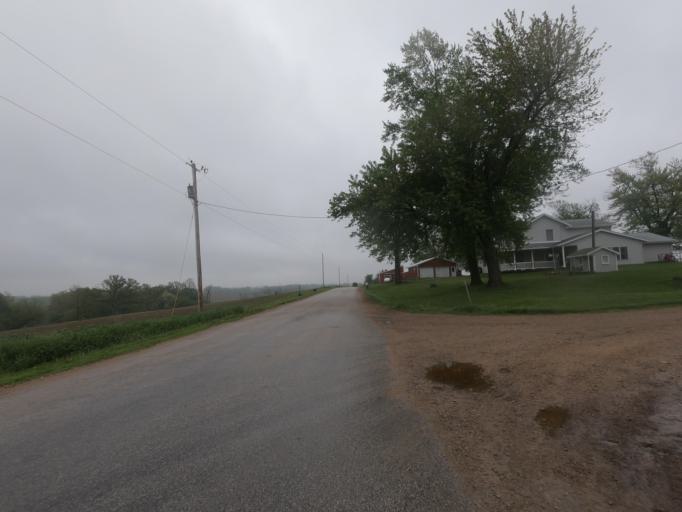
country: US
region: Wisconsin
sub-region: Grant County
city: Hazel Green
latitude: 42.4977
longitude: -90.5039
